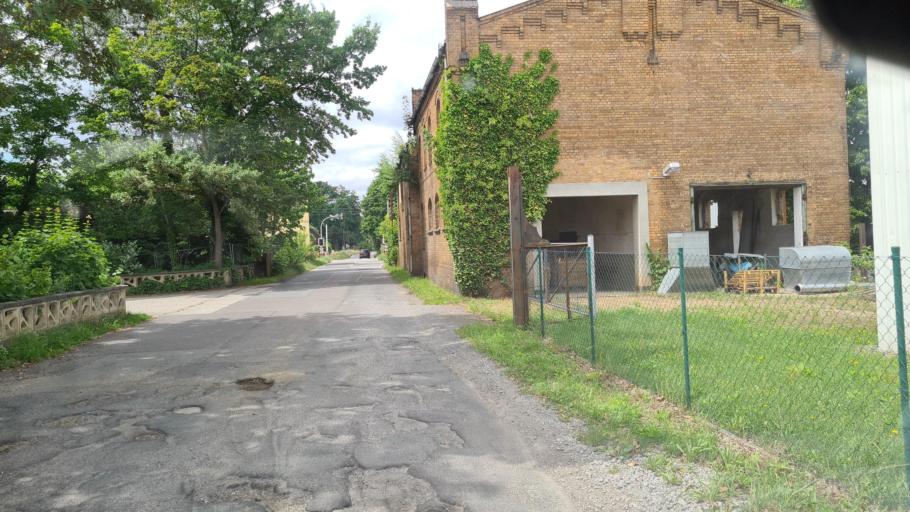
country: DE
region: Brandenburg
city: Grossraschen
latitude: 51.5928
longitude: 14.0160
